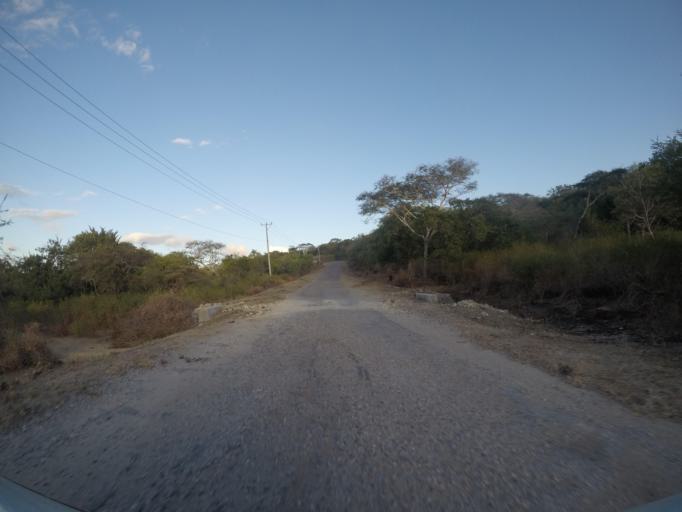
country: TL
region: Lautem
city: Lospalos
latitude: -8.3305
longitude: 127.0037
